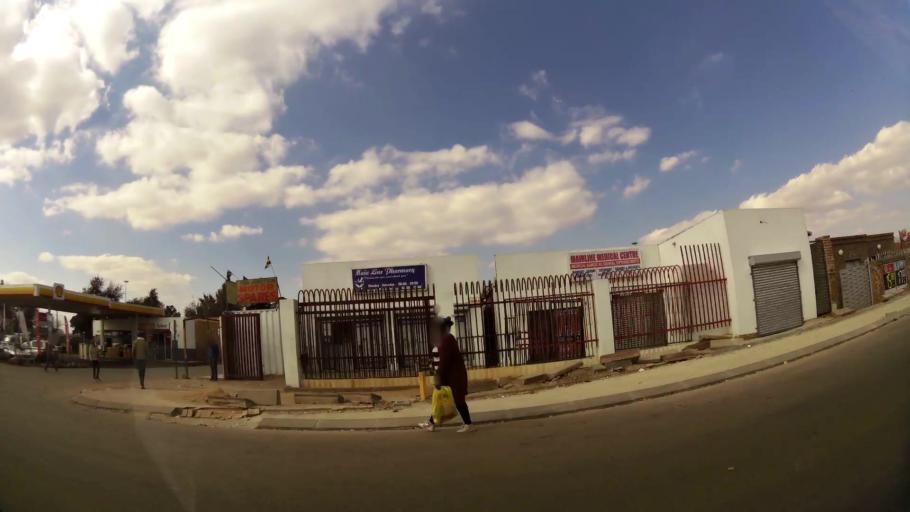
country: ZA
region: Gauteng
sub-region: Ekurhuleni Metropolitan Municipality
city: Tembisa
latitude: -25.9992
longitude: 28.2417
